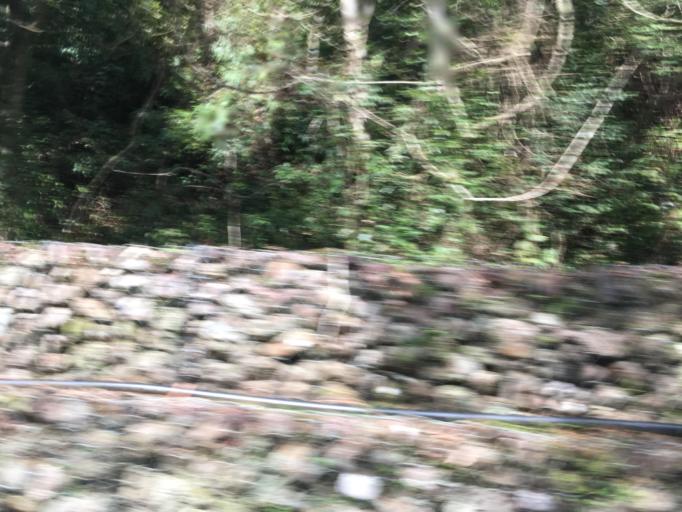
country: TW
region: Taiwan
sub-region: Yilan
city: Yilan
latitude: 24.7598
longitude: 121.5895
